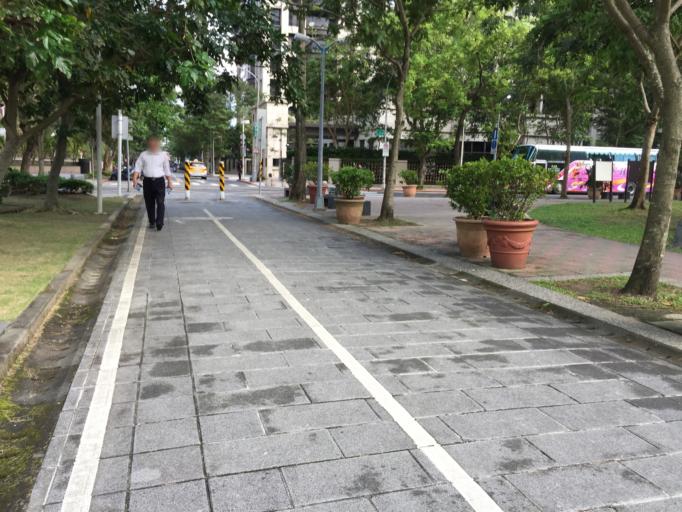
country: TW
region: Taipei
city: Taipei
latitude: 25.0364
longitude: 121.5698
